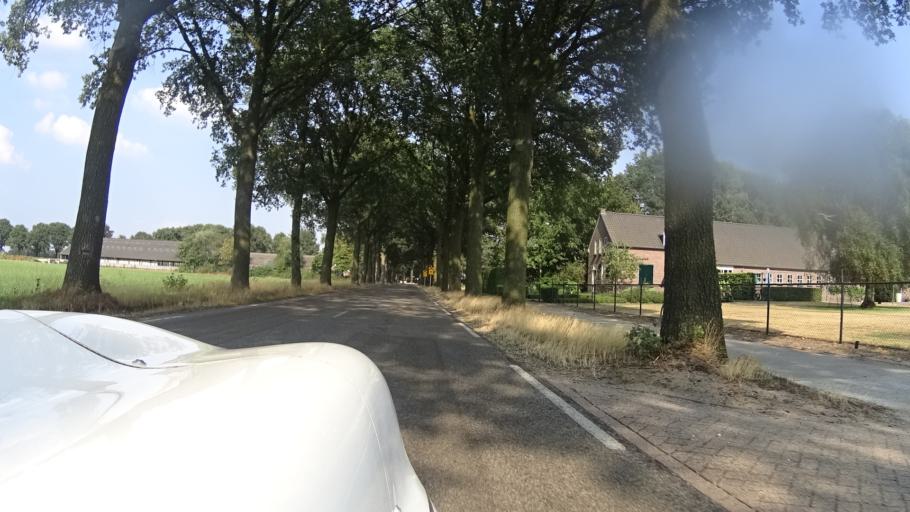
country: NL
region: North Brabant
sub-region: Gemeente Mill en Sint Hubert
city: Wilbertoord
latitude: 51.6150
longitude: 5.7776
